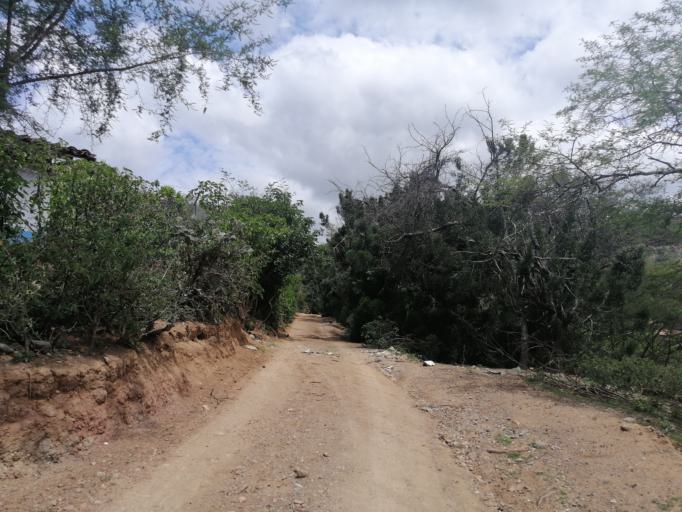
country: EC
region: Loja
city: Catacocha
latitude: -4.0123
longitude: -79.6831
